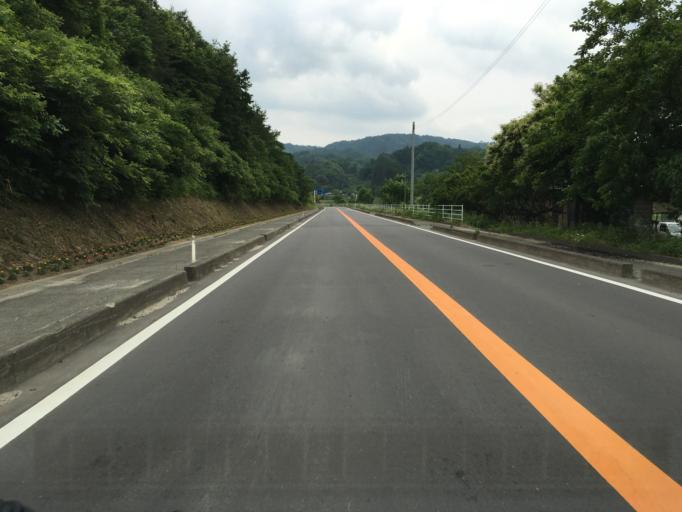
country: JP
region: Fukushima
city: Hobaramachi
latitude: 37.7033
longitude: 140.6072
